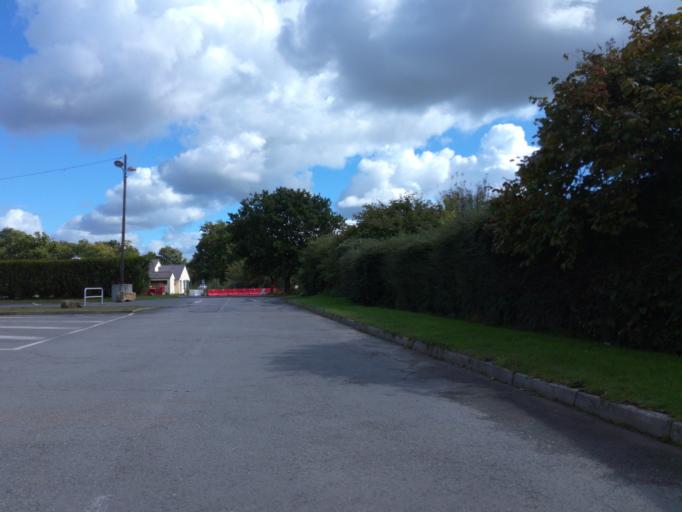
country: FR
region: Brittany
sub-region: Departement d'Ille-et-Vilaine
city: Saint-Aubin-du-Cormier
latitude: 48.2554
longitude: -1.3980
